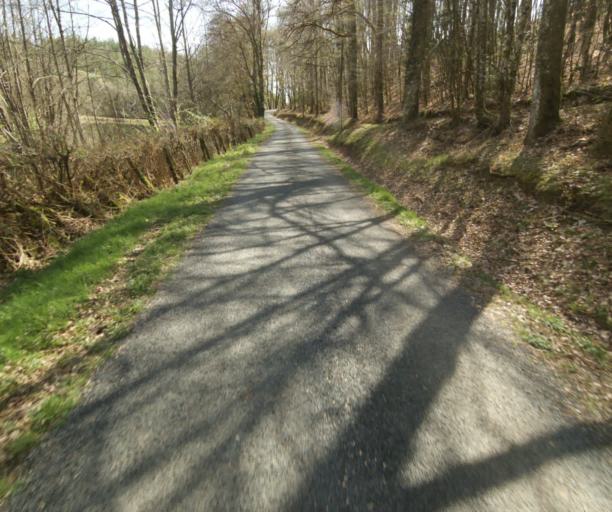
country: FR
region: Limousin
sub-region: Departement de la Correze
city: Seilhac
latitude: 45.4004
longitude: 1.7703
